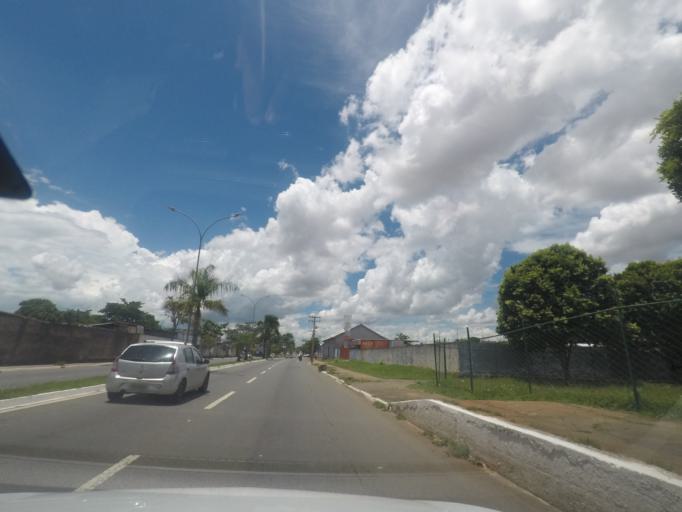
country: BR
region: Goias
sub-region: Goiania
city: Goiania
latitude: -16.6636
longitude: -49.2853
